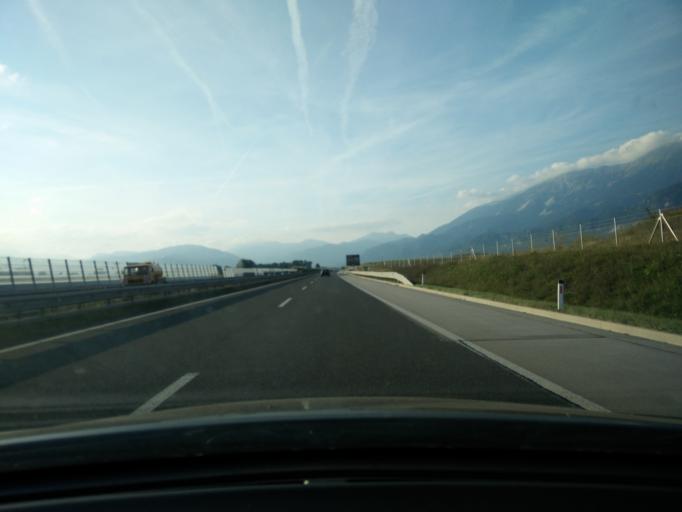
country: SI
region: Radovljica
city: Radovljica
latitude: 46.3475
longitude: 14.1813
